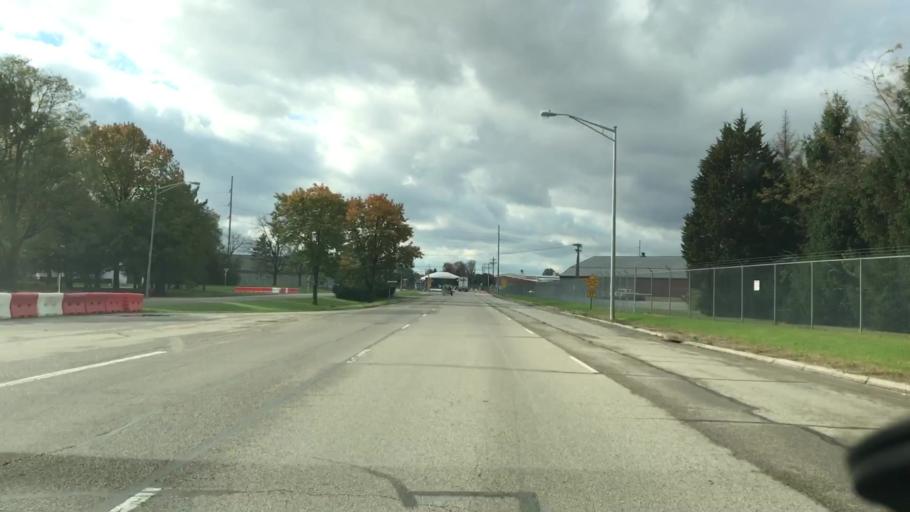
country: US
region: Ohio
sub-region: Greene County
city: Fairborn
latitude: 39.8183
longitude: -84.0291
